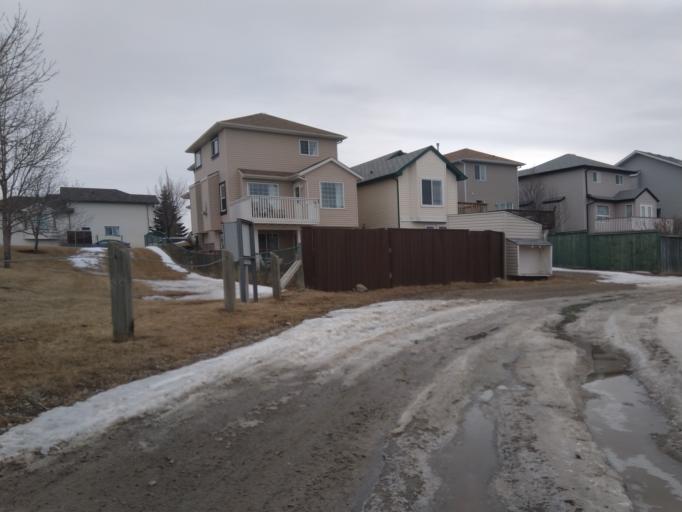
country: CA
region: Alberta
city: Calgary
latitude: 51.1682
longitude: -114.0441
